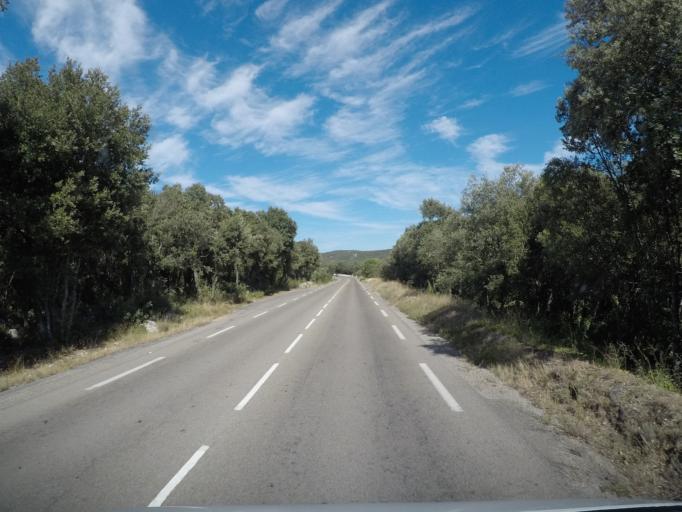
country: FR
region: Languedoc-Roussillon
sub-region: Departement du Gard
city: Sauve
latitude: 43.9679
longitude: 3.9217
